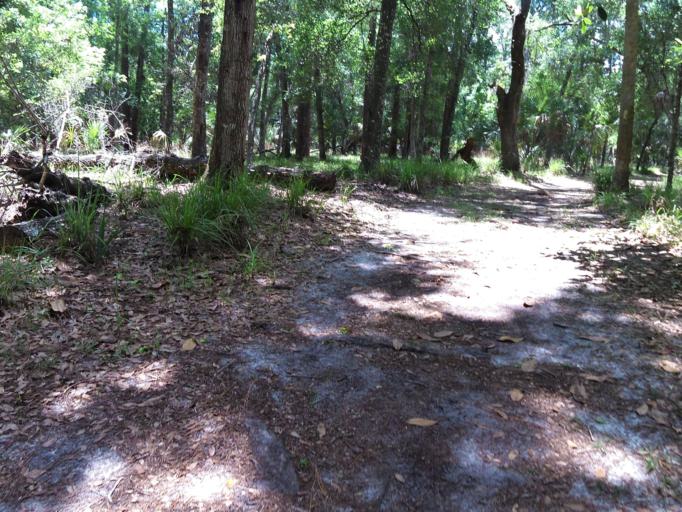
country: US
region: Florida
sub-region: Flagler County
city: Flagler Beach
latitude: 29.4321
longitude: -81.1403
